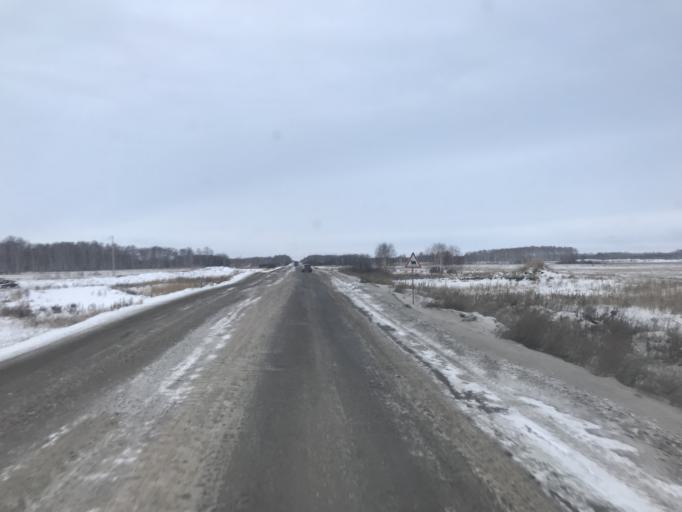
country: KZ
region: Soltustik Qazaqstan
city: Bishkul
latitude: 54.9203
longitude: 68.7689
